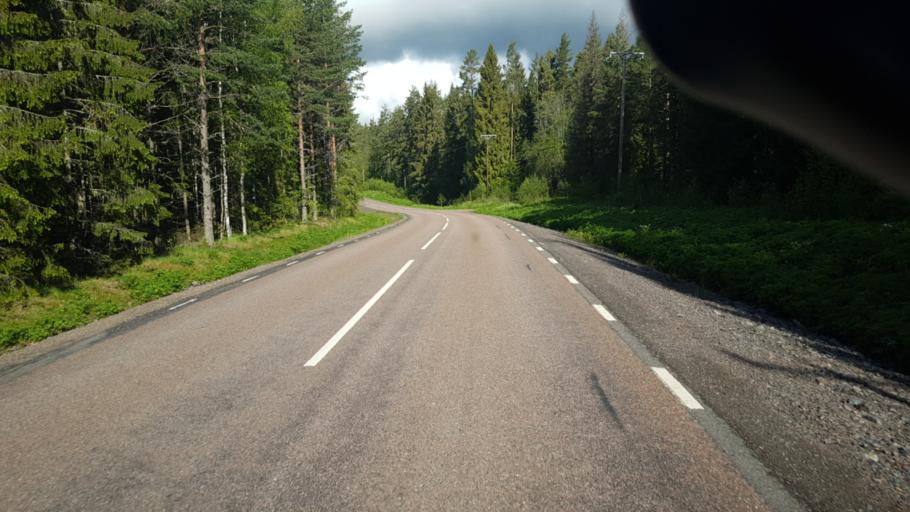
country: SE
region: Vaermland
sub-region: Eda Kommun
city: Charlottenberg
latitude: 59.8075
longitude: 12.2050
